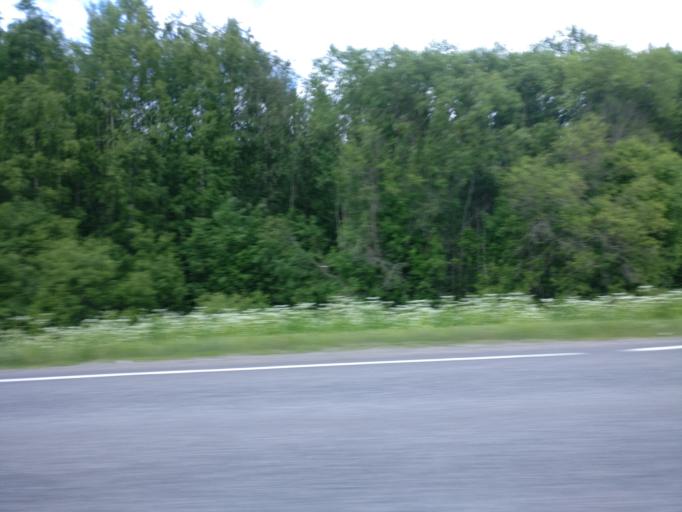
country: FI
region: Southern Savonia
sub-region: Savonlinna
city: Savonlinna
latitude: 61.9079
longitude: 28.9277
